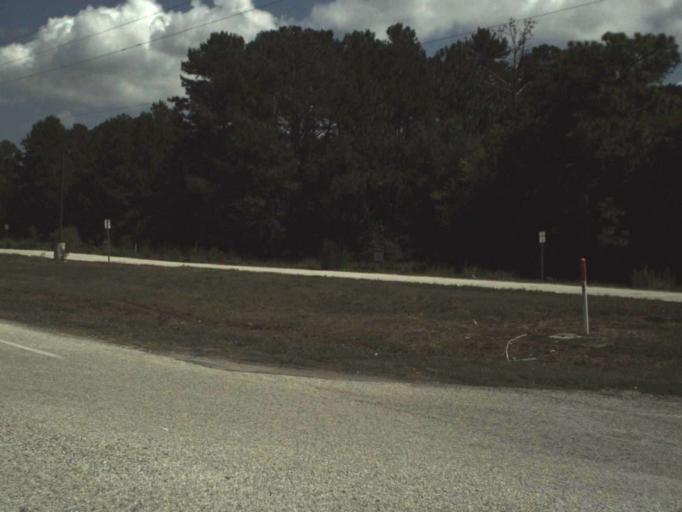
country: US
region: Florida
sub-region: Lake County
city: Mount Dora
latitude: 28.8161
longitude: -81.6294
